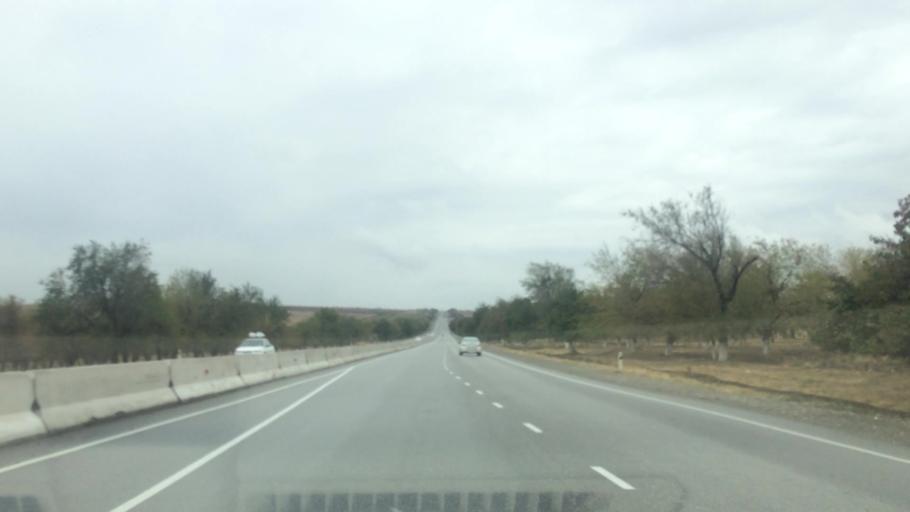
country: UZ
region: Samarqand
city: Bulung'ur
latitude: 39.8763
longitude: 67.4822
